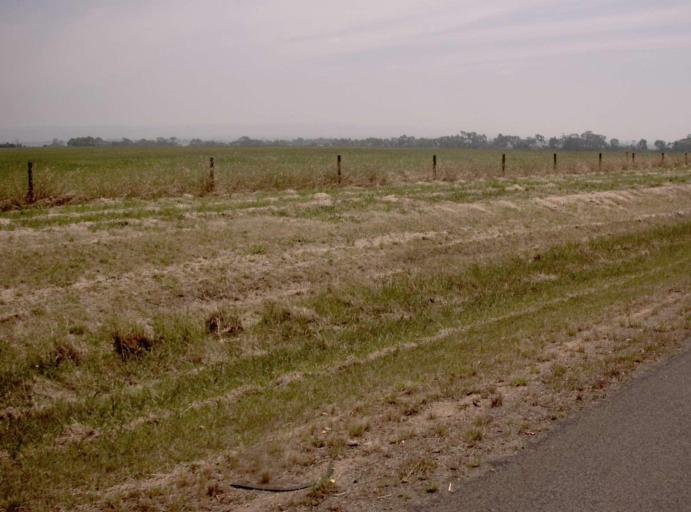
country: AU
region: Victoria
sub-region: Latrobe
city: Traralgon
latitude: -38.2464
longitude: 146.6233
